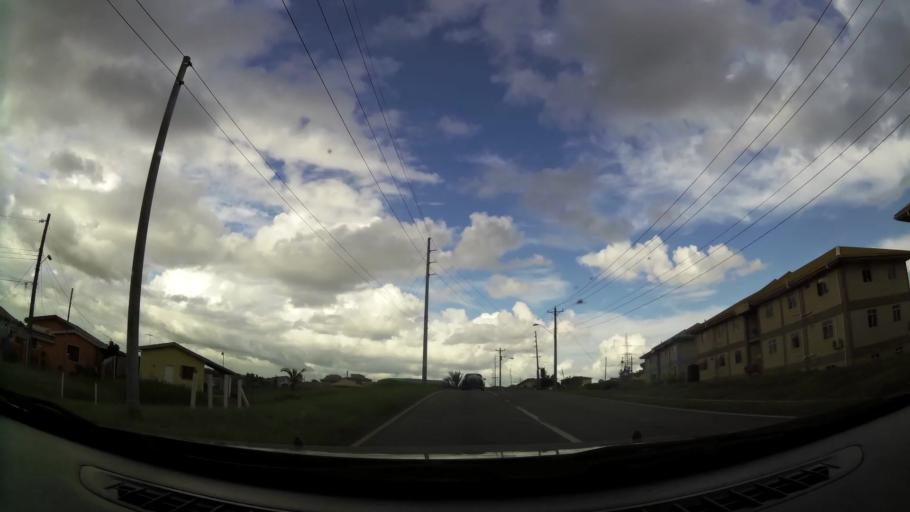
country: TT
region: City of San Fernando
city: Mon Repos
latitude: 10.2664
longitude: -61.4430
